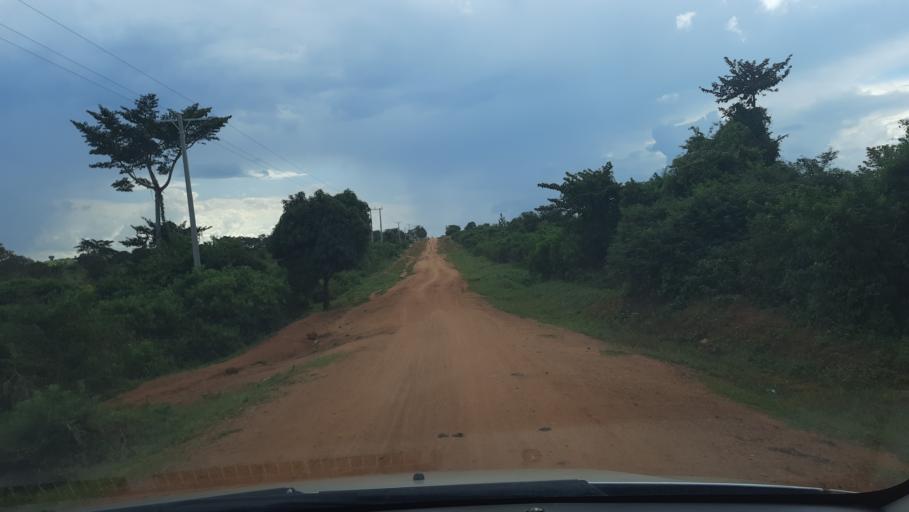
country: UG
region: Central Region
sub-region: Nakasongola District
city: Nakasongola
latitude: 1.3802
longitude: 32.5054
